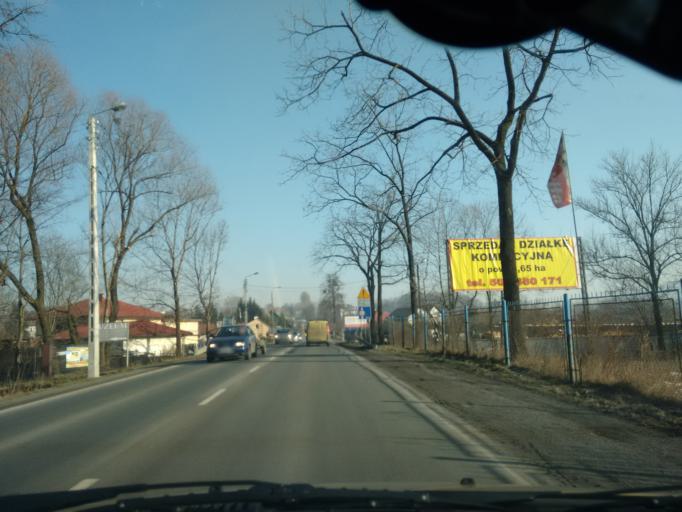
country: PL
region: Lesser Poland Voivodeship
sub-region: Powiat wadowicki
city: Jaroszowice
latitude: 49.8755
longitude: 19.5173
